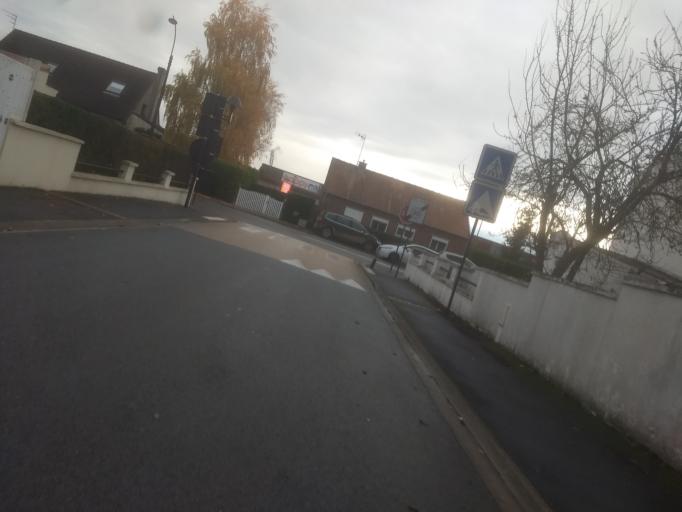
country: FR
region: Nord-Pas-de-Calais
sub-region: Departement du Pas-de-Calais
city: Dainville
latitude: 50.2864
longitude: 2.7420
